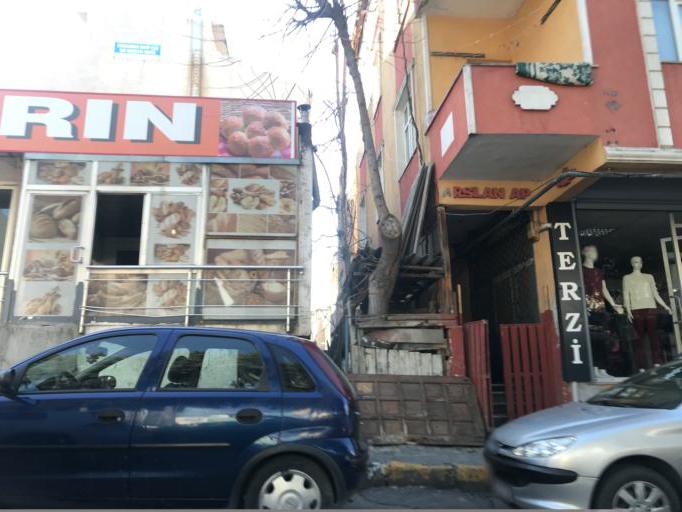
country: TR
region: Istanbul
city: Mahmutbey
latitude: 41.0330
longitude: 28.7746
